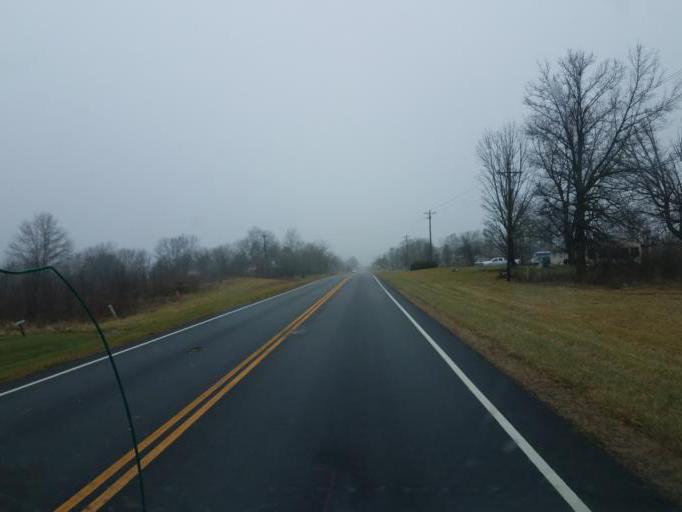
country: US
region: Ohio
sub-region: Champaign County
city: North Lewisburg
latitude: 40.2623
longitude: -83.4656
